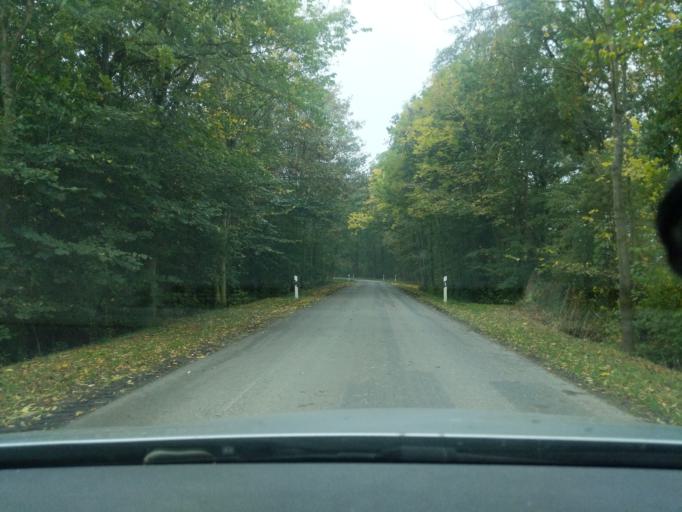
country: DE
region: Lower Saxony
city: Nordleda
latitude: 53.8268
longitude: 8.8267
